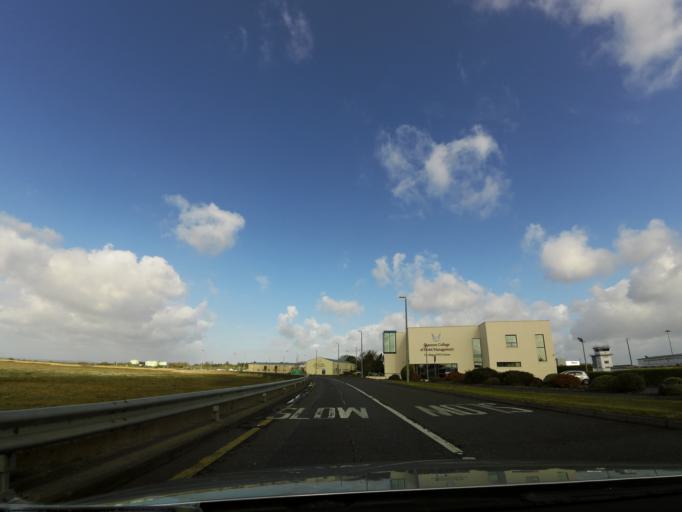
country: IE
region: Munster
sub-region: An Clar
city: Shannon
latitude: 52.6898
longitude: -8.9163
